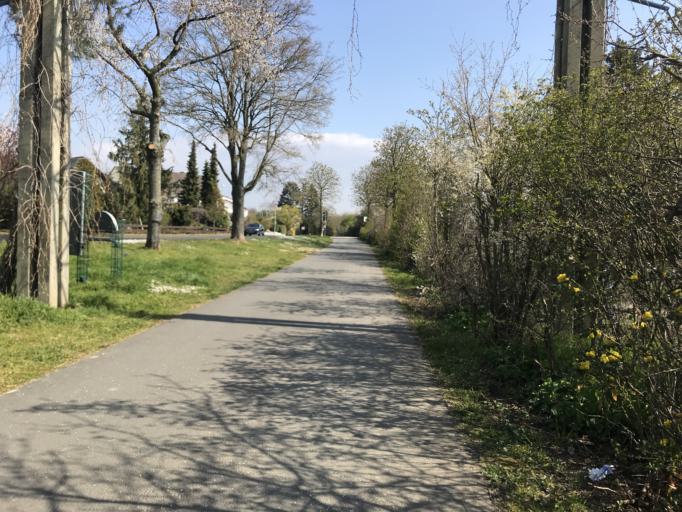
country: DE
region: Hesse
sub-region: Regierungsbezirk Darmstadt
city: Florsheim
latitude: 50.0252
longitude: 8.4122
